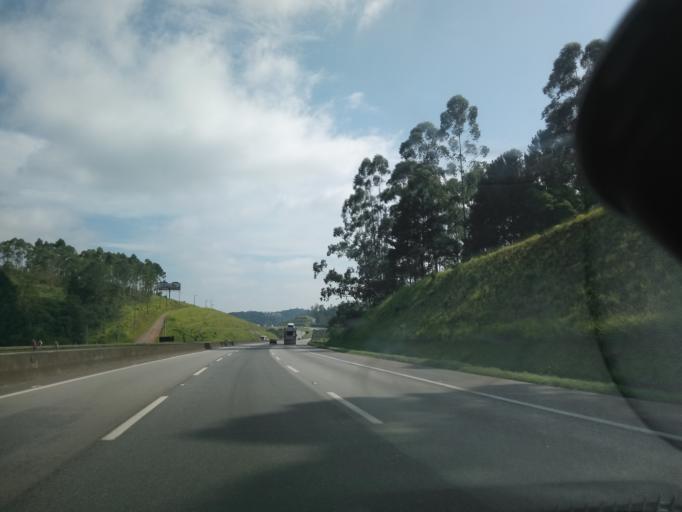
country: BR
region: Sao Paulo
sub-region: Itapecerica Da Serra
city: Itapecerica da Serra
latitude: -23.7361
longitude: -46.8126
